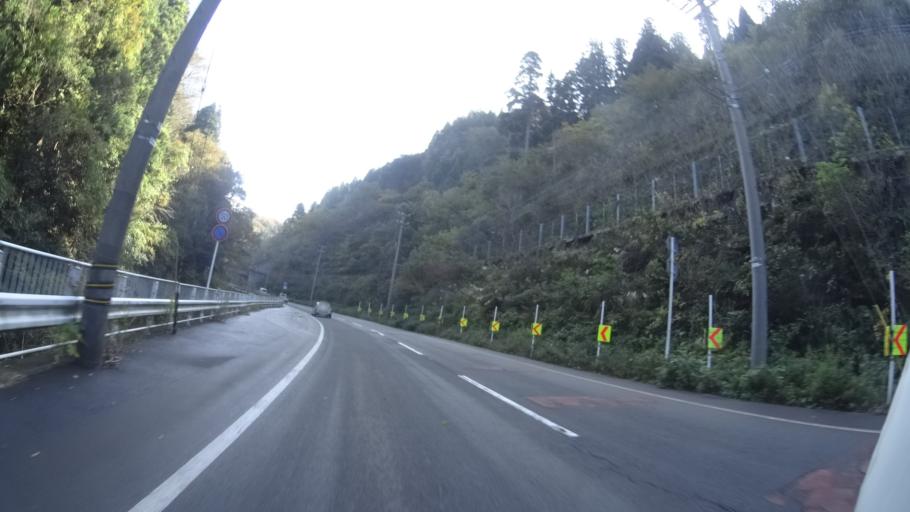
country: JP
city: Asahi
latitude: 35.9578
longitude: 135.9990
